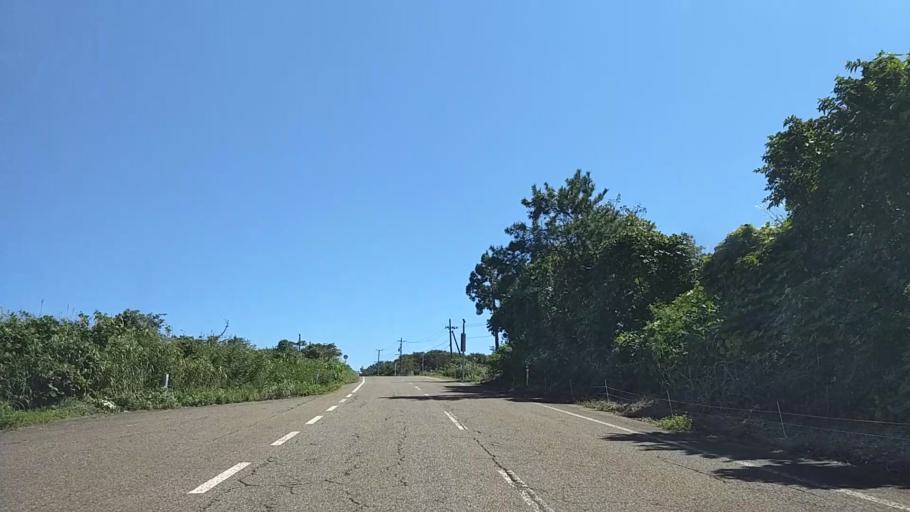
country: JP
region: Niigata
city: Joetsu
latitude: 37.1712
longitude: 138.1041
